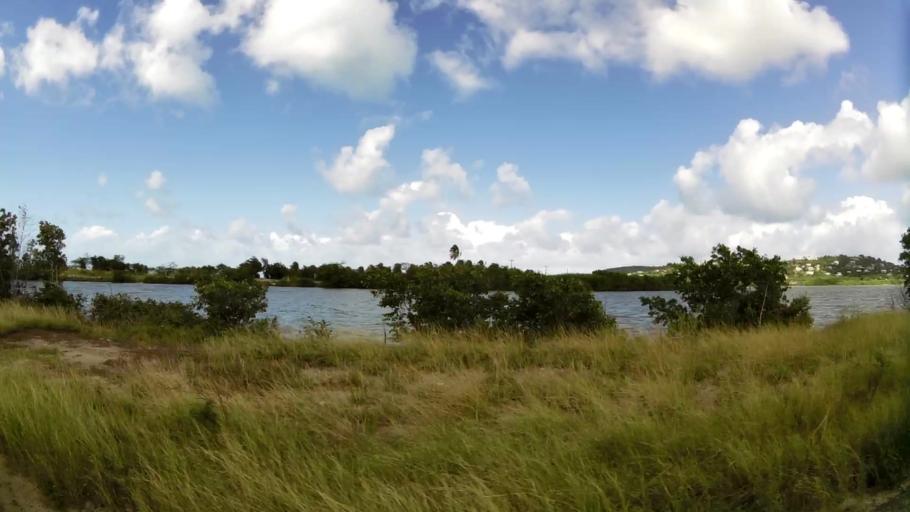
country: AG
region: Saint John
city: Saint John's
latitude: 17.1457
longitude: -61.8555
